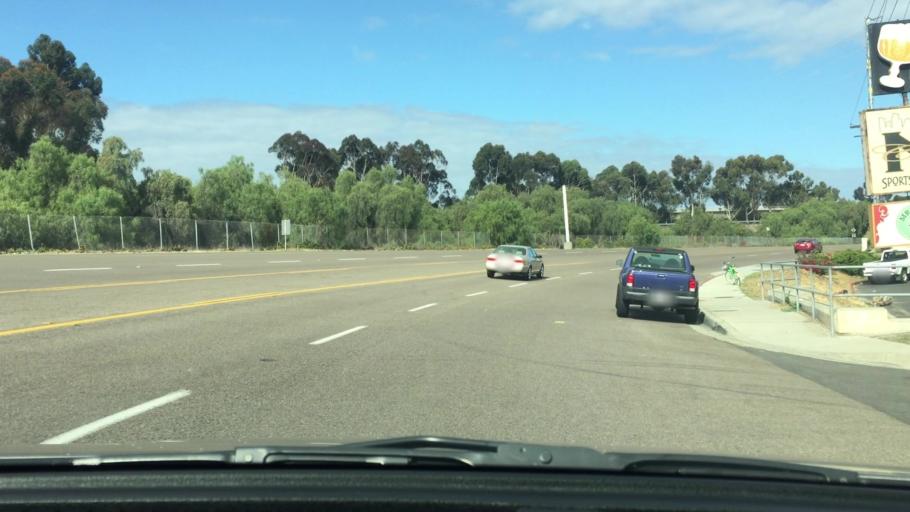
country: US
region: California
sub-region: San Diego County
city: Chula Vista
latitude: 32.6600
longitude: -117.0717
